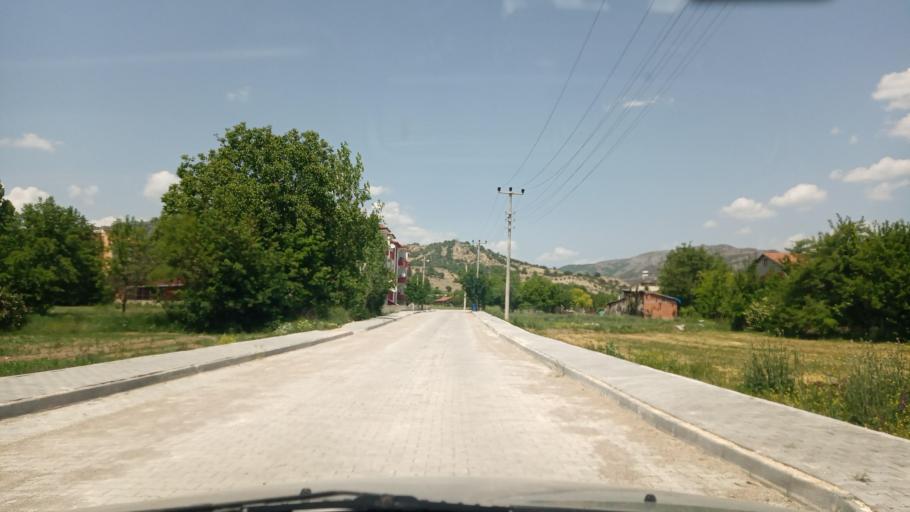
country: TR
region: Bolu
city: Seben
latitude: 40.4136
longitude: 31.5778
